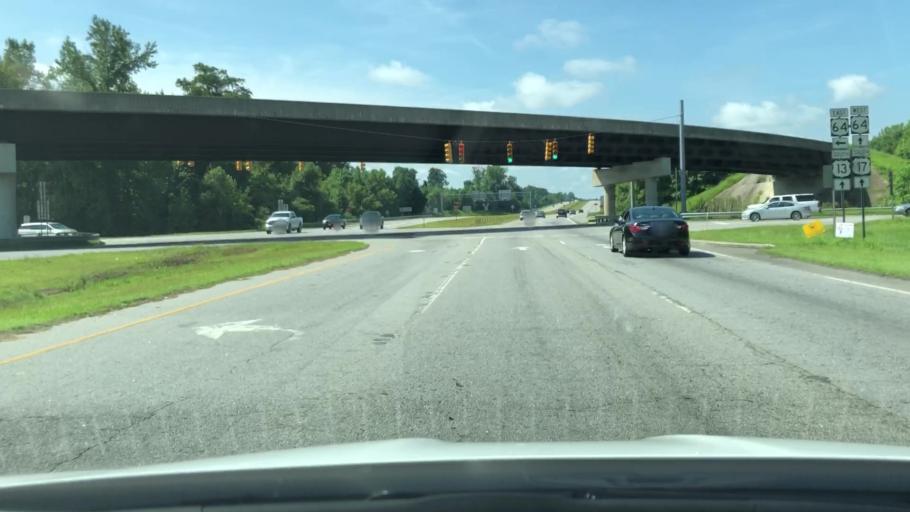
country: US
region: North Carolina
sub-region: Martin County
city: Williamston
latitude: 35.8415
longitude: -77.0525
